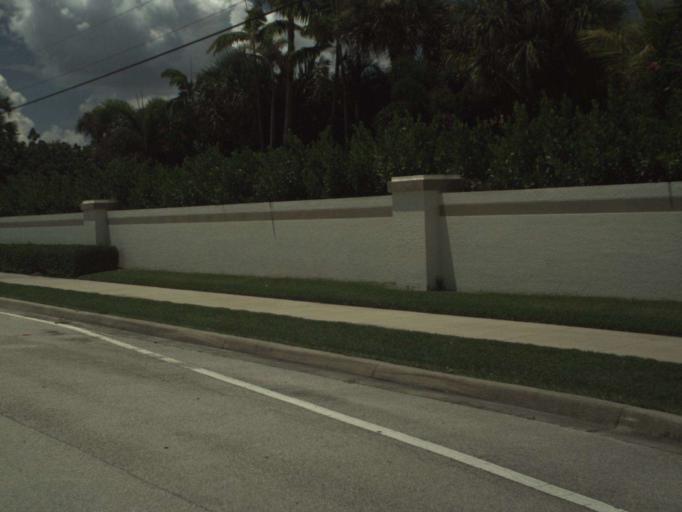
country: US
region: Florida
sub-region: Martin County
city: Sewall's Point
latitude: 27.2321
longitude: -80.1851
